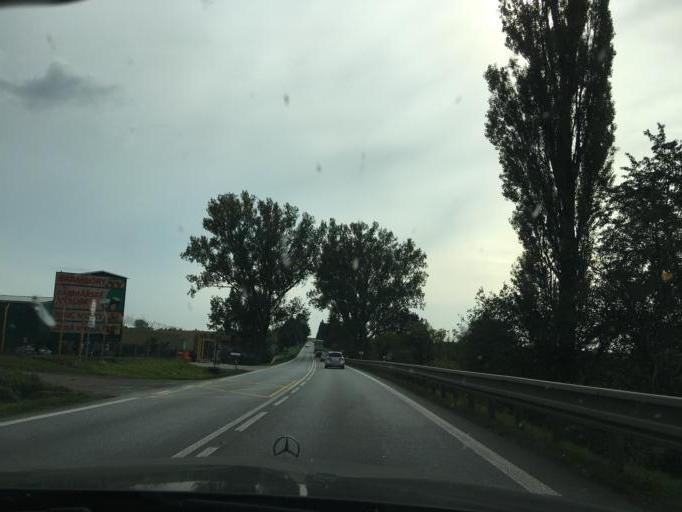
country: CZ
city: Predmerice nad Labem
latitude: 50.2817
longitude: 15.8191
